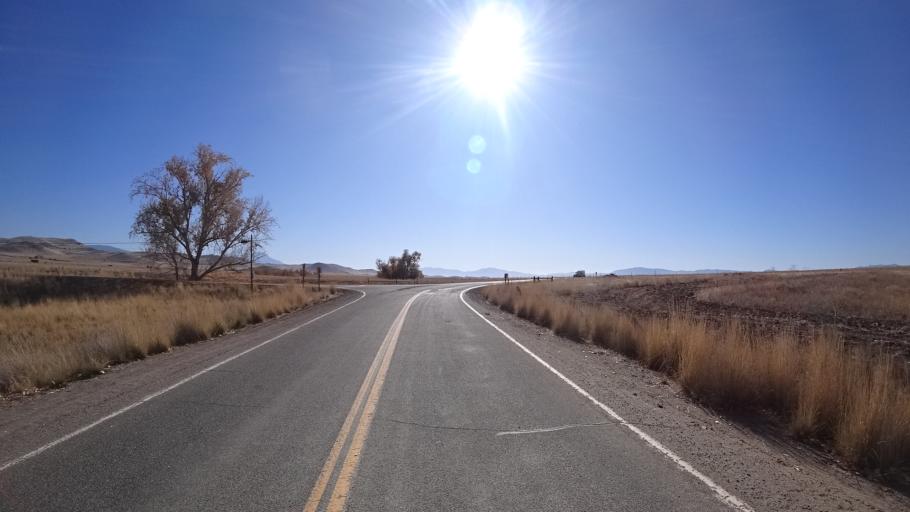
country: US
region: California
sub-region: Siskiyou County
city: Montague
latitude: 41.8088
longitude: -122.4402
